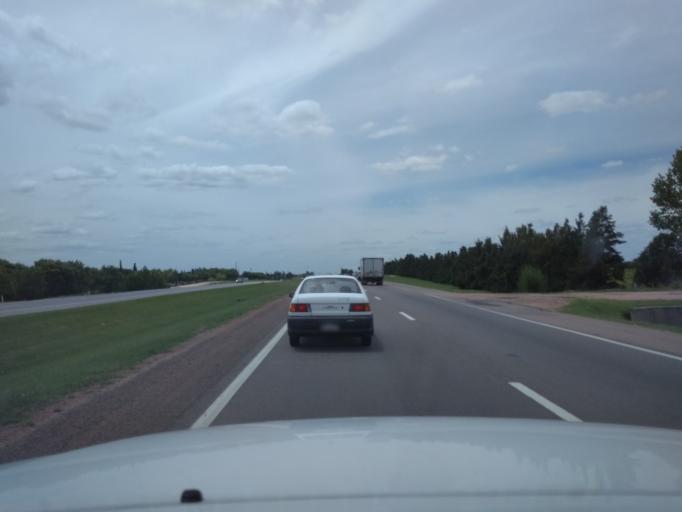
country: UY
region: Canelones
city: La Paz
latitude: -34.7412
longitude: -56.2515
